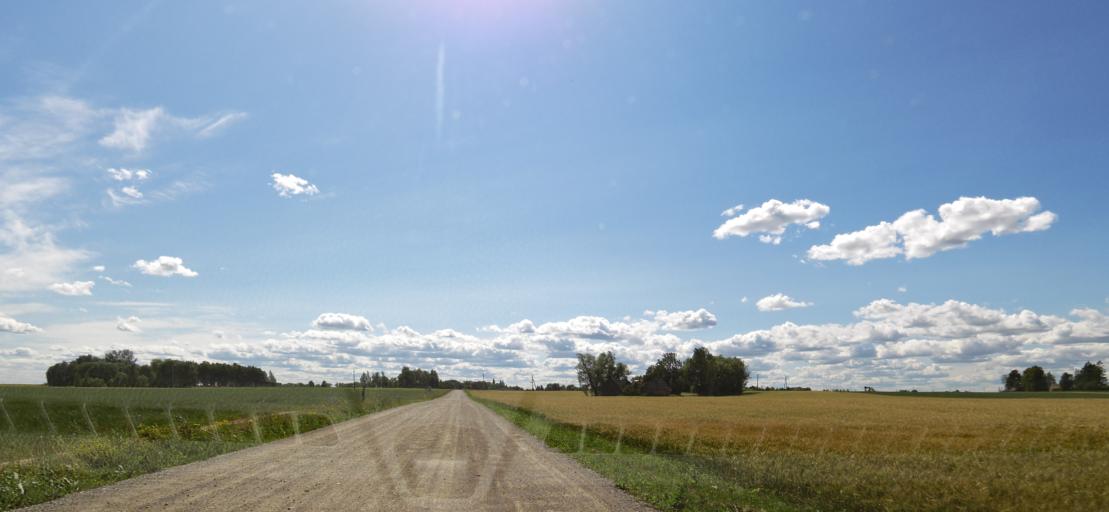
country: LV
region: Bauskas Rajons
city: Bauska
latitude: 56.2409
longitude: 24.2445
